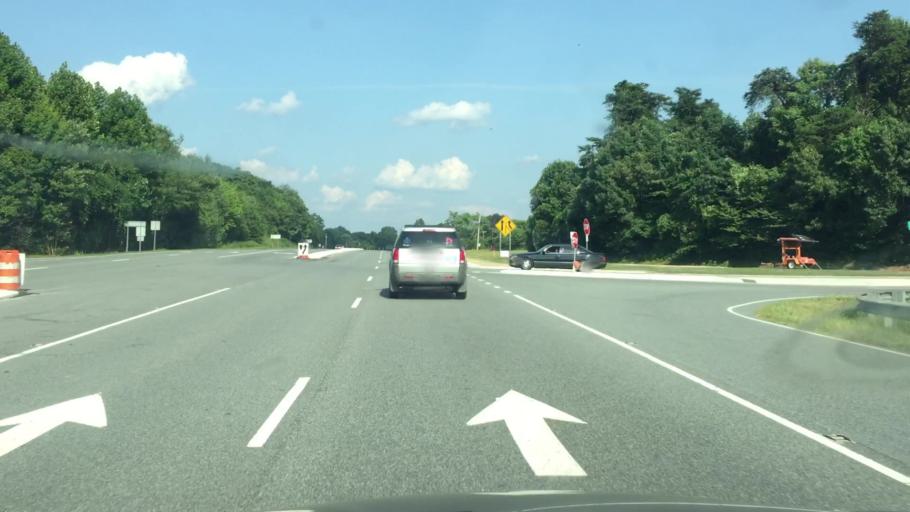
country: US
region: North Carolina
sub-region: Rockingham County
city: Reidsville
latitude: 36.3612
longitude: -79.6334
